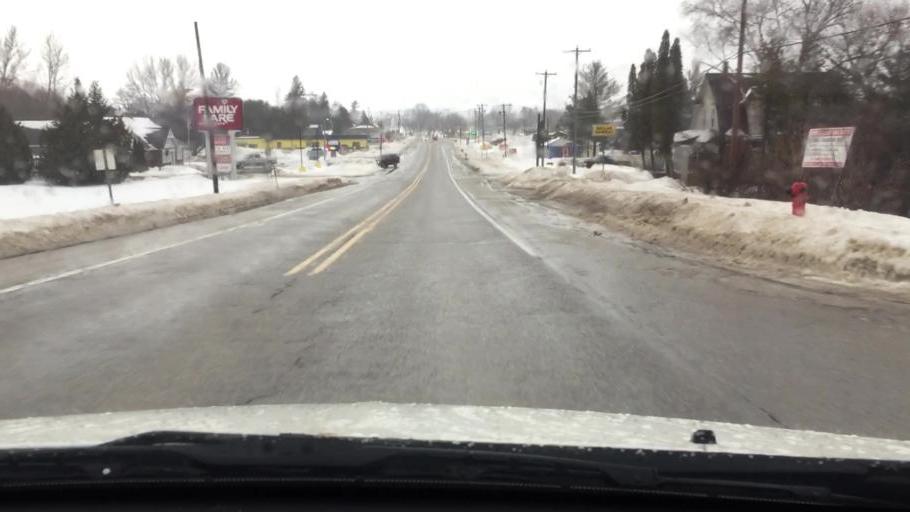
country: US
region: Michigan
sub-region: Charlevoix County
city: East Jordan
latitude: 45.1506
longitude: -85.1399
